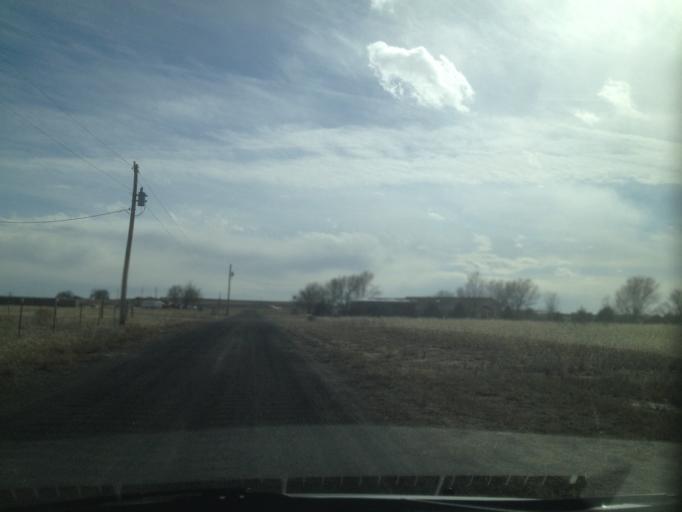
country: US
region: Colorado
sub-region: Weld County
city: Kersey
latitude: 40.2901
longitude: -104.2626
